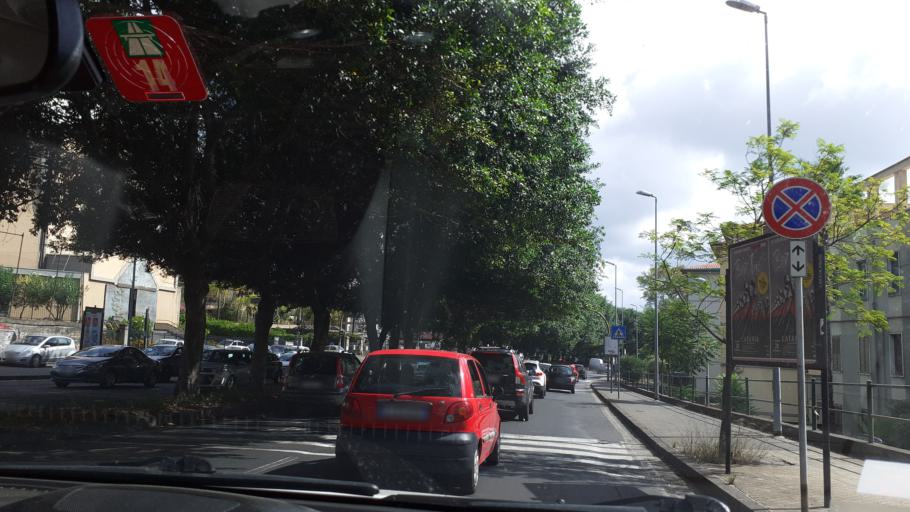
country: IT
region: Sicily
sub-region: Catania
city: Canalicchio
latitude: 37.5274
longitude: 15.0840
